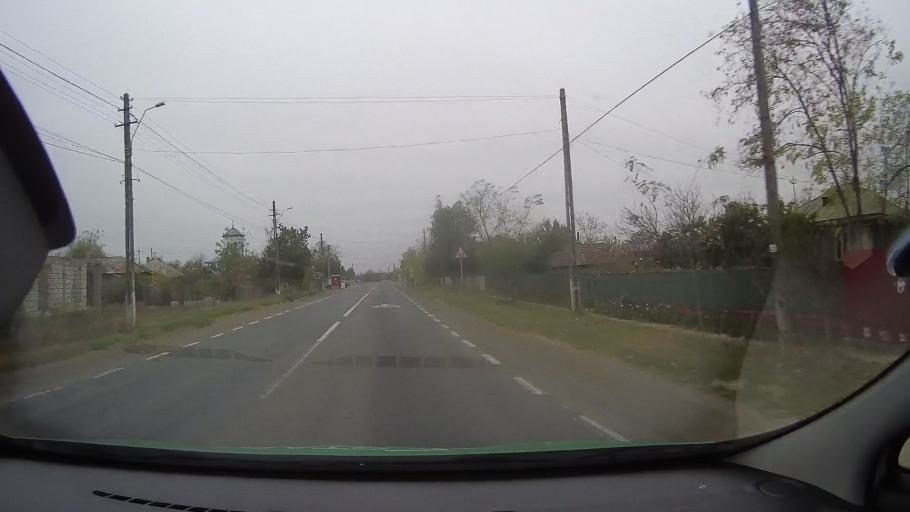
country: RO
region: Braila
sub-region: Comuna Baraganul
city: Baraganul
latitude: 44.8045
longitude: 27.5133
